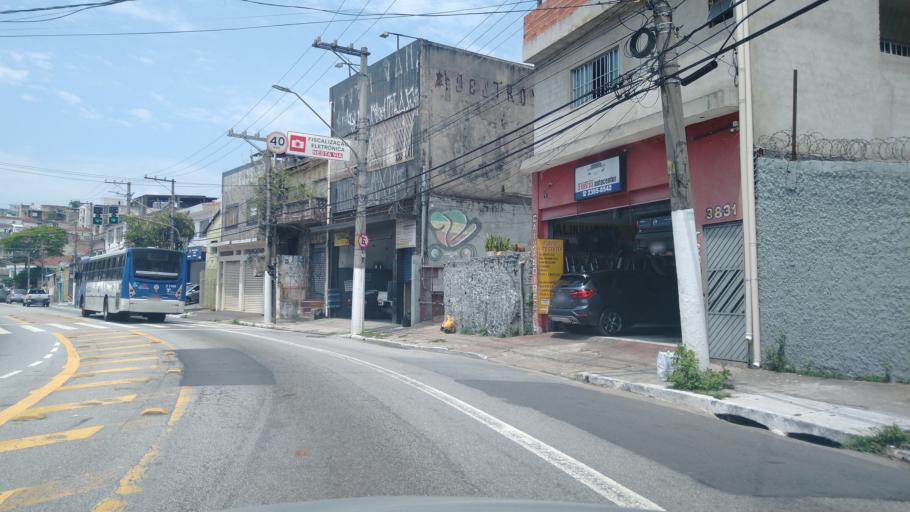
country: BR
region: Sao Paulo
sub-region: Sao Paulo
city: Sao Paulo
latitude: -23.4786
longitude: -46.6626
